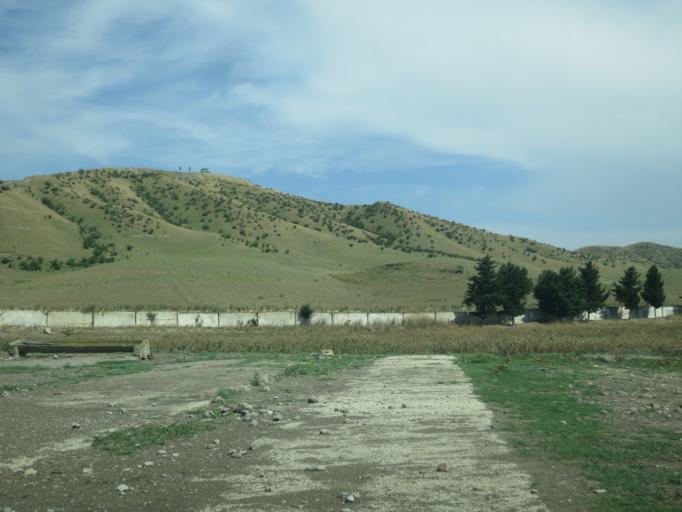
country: GE
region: Kvemo Kartli
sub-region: Gardabani
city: Gardabani
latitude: 41.4989
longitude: 45.1881
